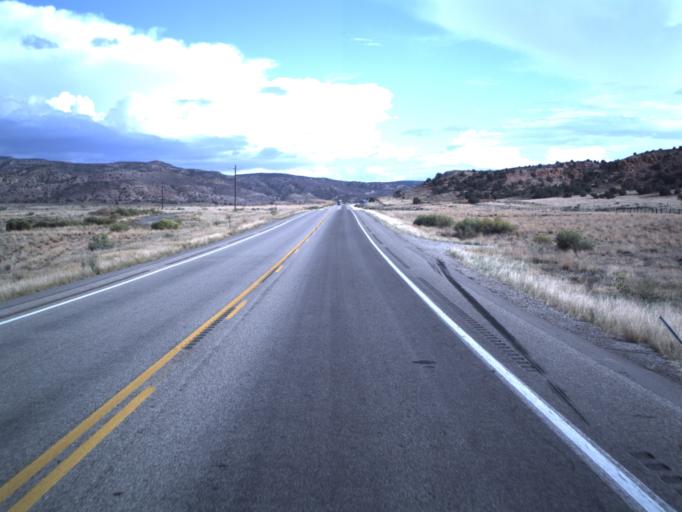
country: US
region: Utah
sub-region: Grand County
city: Moab
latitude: 38.4507
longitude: -109.4376
